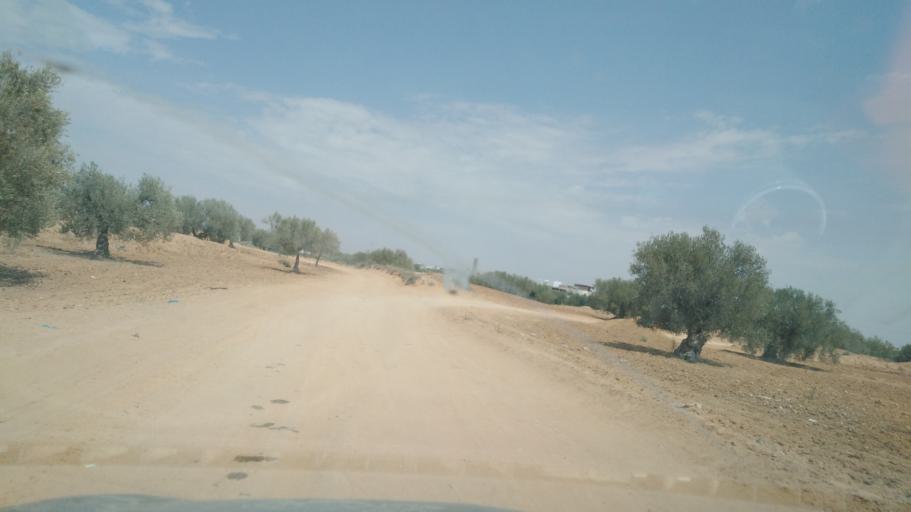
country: TN
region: Safaqis
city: Sfax
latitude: 34.7388
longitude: 10.5595
